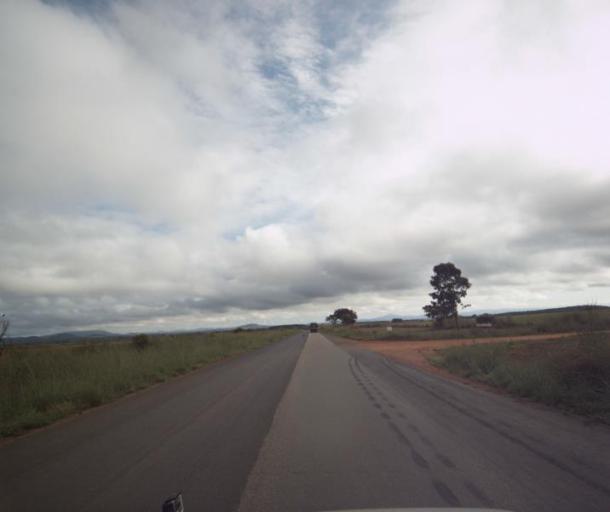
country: BR
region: Goias
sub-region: Padre Bernardo
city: Padre Bernardo
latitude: -15.3539
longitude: -48.6467
